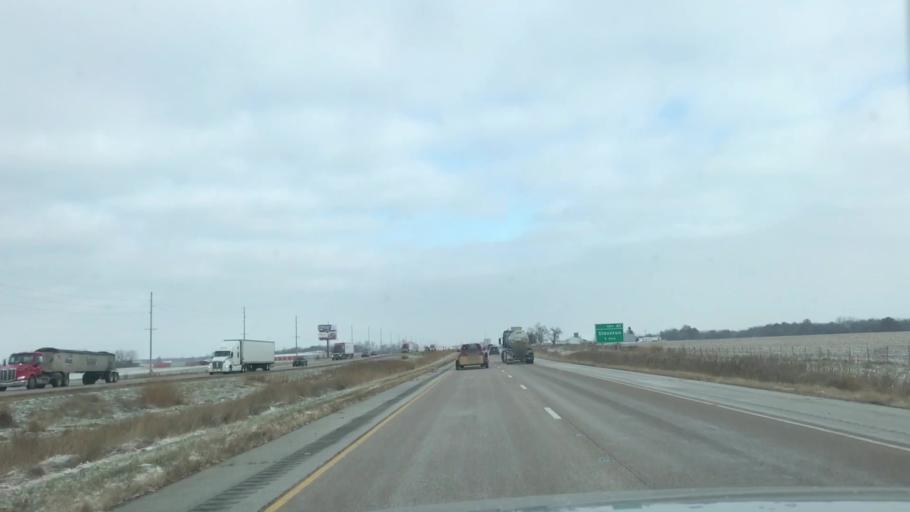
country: US
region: Illinois
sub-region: Macoupin County
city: Staunton
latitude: 39.0000
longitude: -89.7496
